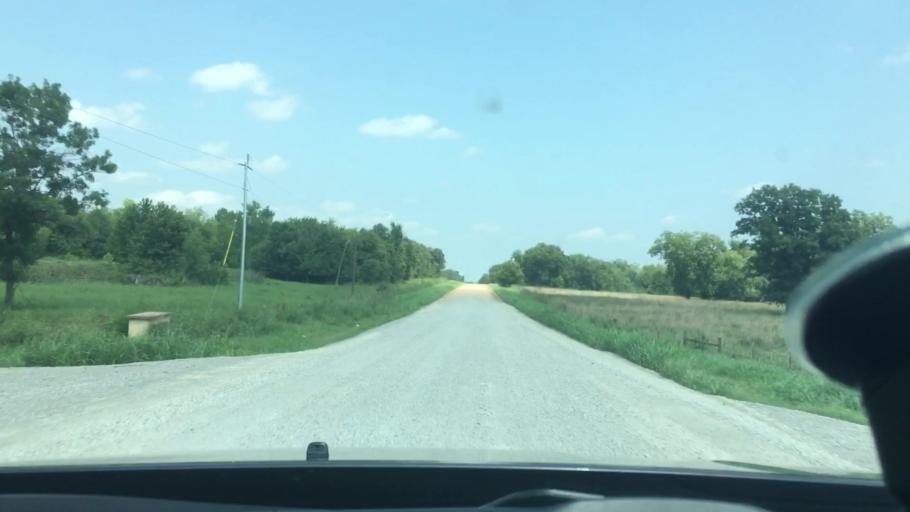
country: US
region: Oklahoma
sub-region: Coal County
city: Coalgate
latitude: 34.4277
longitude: -96.4613
